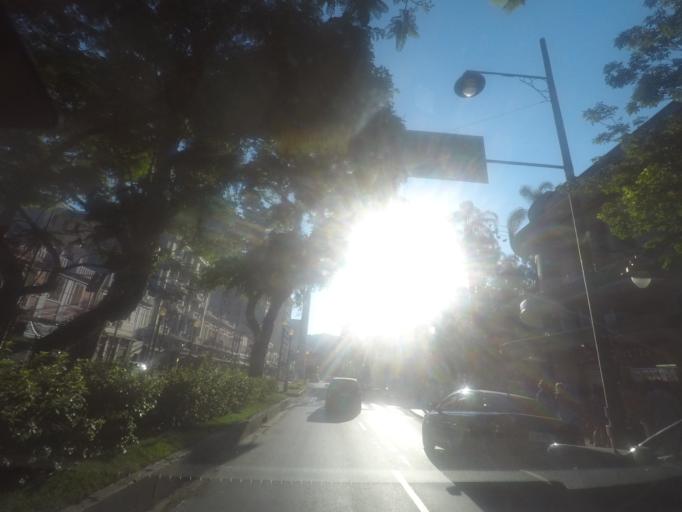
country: BR
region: Rio de Janeiro
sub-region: Petropolis
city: Petropolis
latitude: -22.5097
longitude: -43.1747
